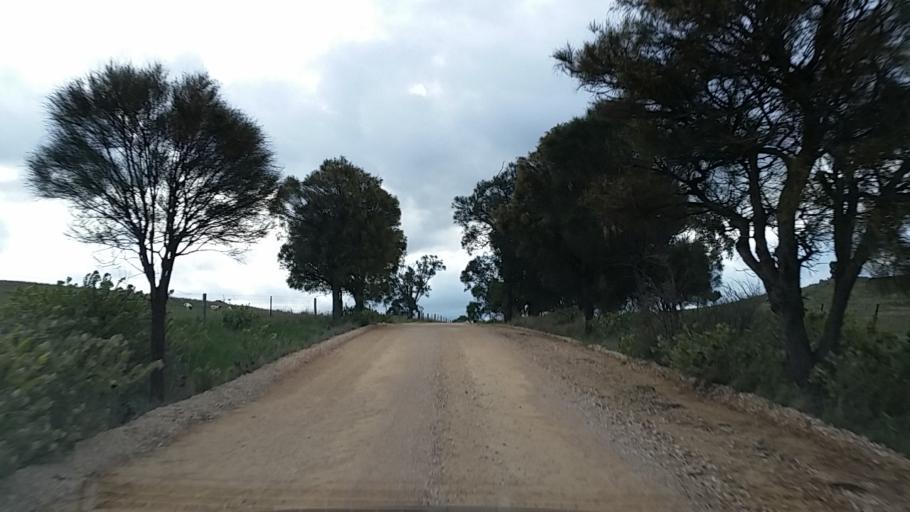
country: AU
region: South Australia
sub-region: Mount Barker
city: Callington
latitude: -34.9720
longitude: 139.0560
